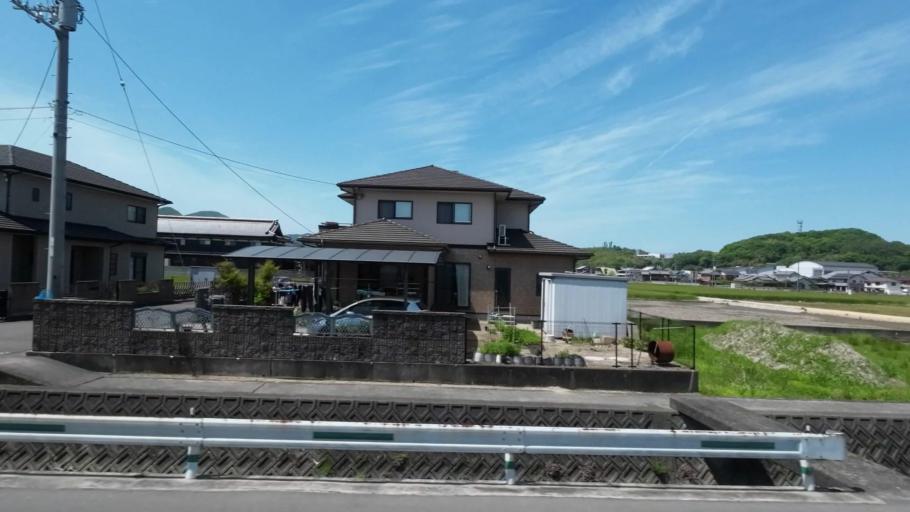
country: JP
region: Kagawa
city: Tadotsu
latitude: 34.2643
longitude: 133.7547
